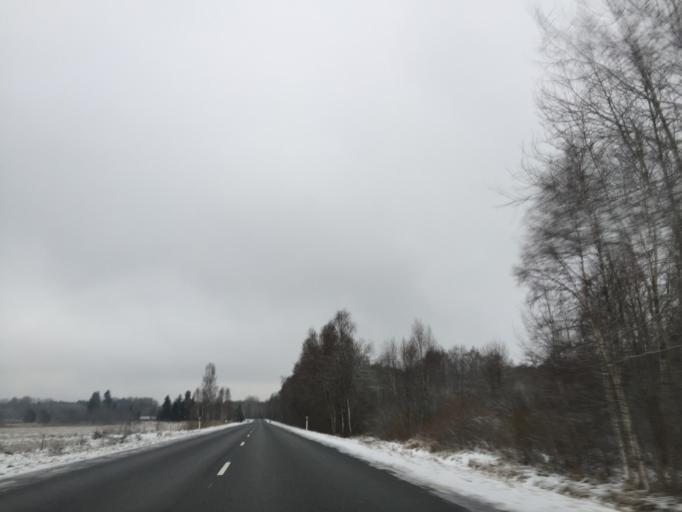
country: EE
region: Laeaene
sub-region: Lihula vald
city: Lihula
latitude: 58.6578
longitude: 23.8367
